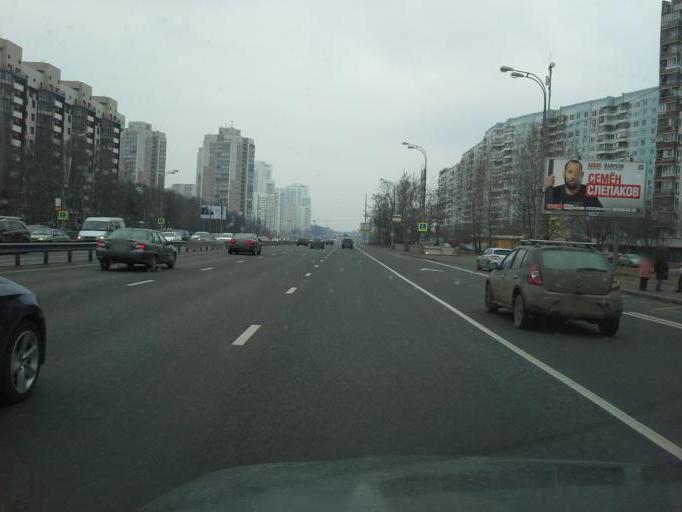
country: RU
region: Moscow
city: Troparevo
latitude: 55.6533
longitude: 37.4905
